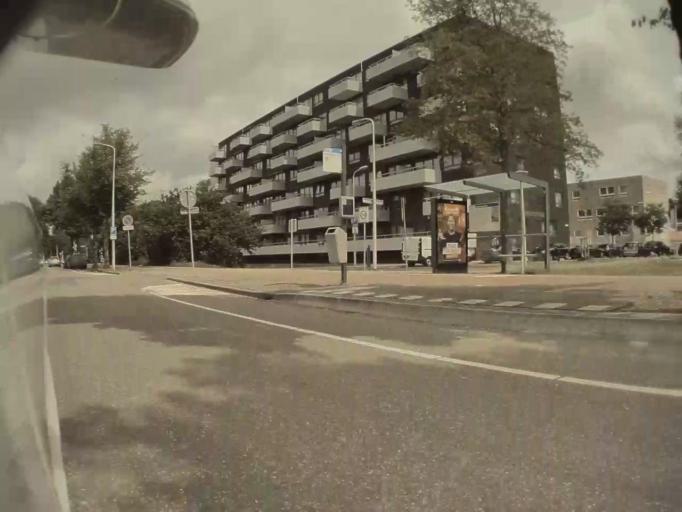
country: NL
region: South Holland
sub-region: Gemeente Westland
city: Kwintsheul
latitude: 52.0390
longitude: 4.2680
